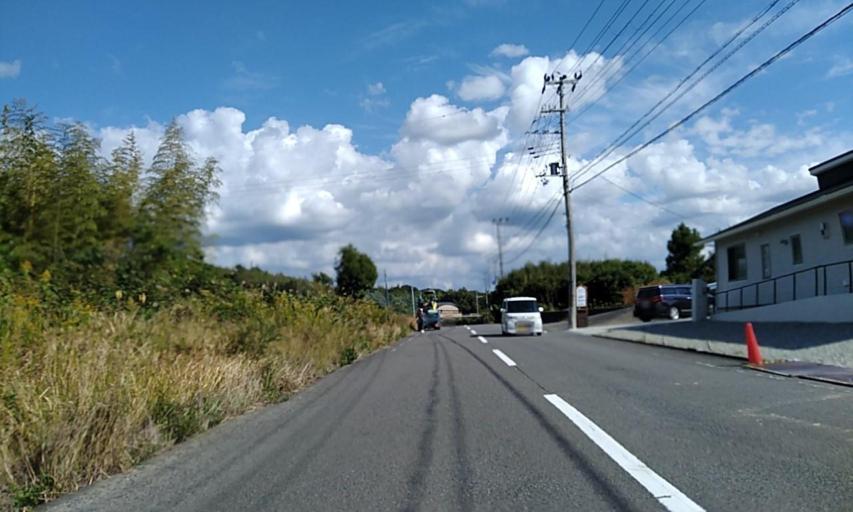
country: JP
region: Wakayama
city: Gobo
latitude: 33.8892
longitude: 135.1737
